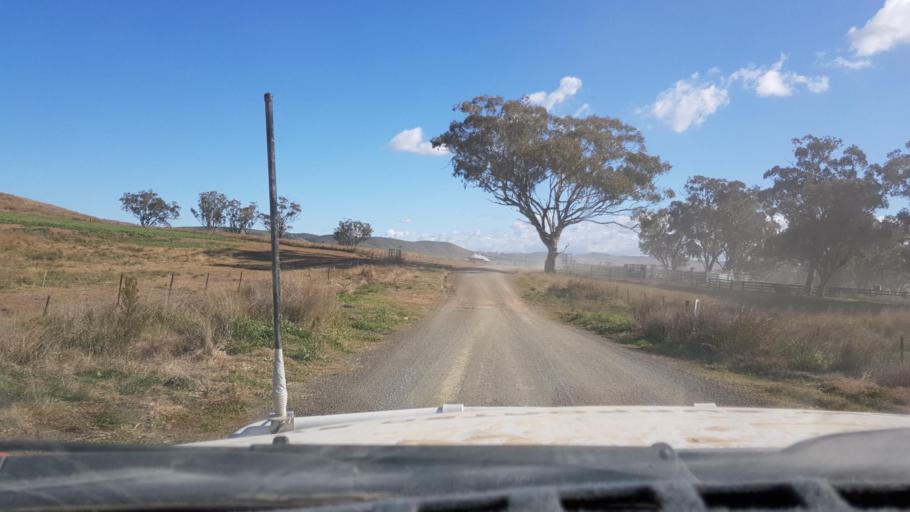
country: AU
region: New South Wales
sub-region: Narrabri
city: Blair Athol
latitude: -30.5379
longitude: 150.4497
